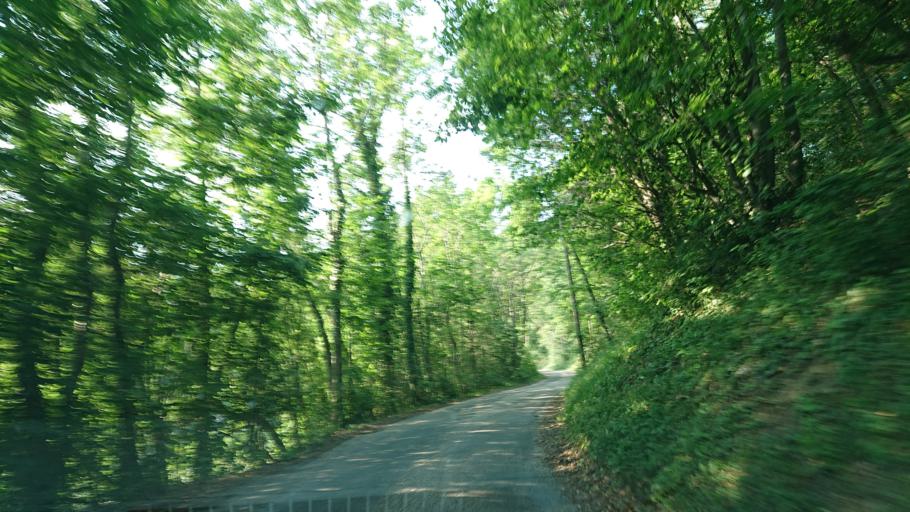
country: FR
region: Rhone-Alpes
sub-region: Departement de l'Isere
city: La Mure
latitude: 44.8166
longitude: 5.9364
